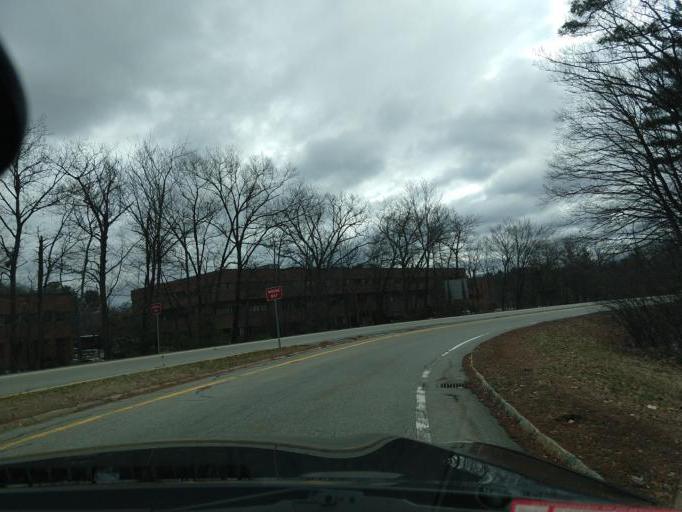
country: US
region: Massachusetts
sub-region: Middlesex County
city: Billerica
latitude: 42.5439
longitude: -71.2823
